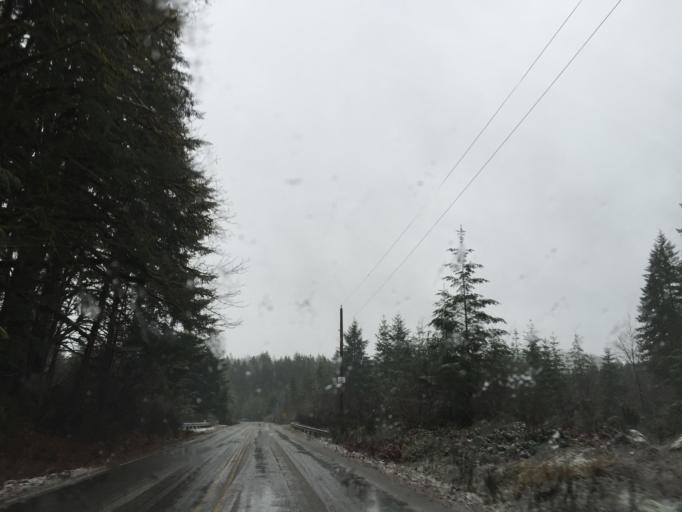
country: US
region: Washington
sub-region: Thurston County
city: Rochester
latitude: 46.9480
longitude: -123.0725
